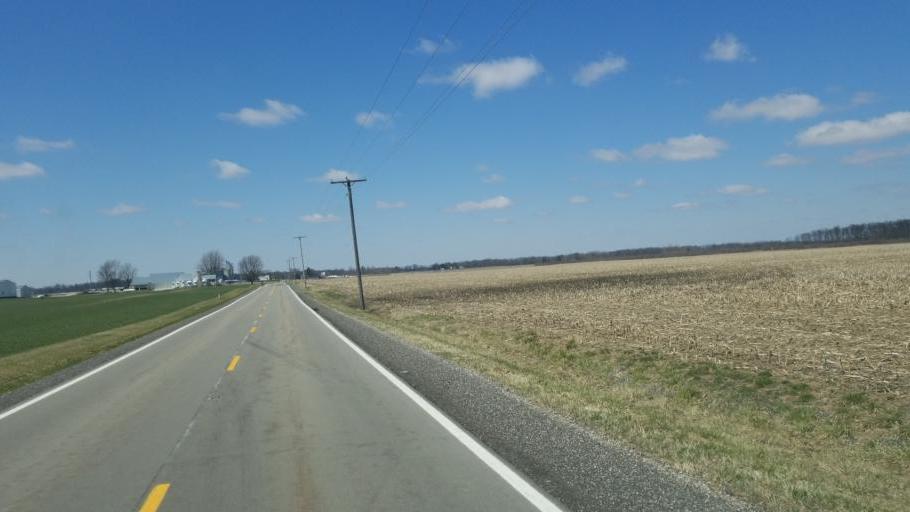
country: US
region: Ohio
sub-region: Crawford County
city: Bucyrus
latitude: 40.7177
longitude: -83.0211
